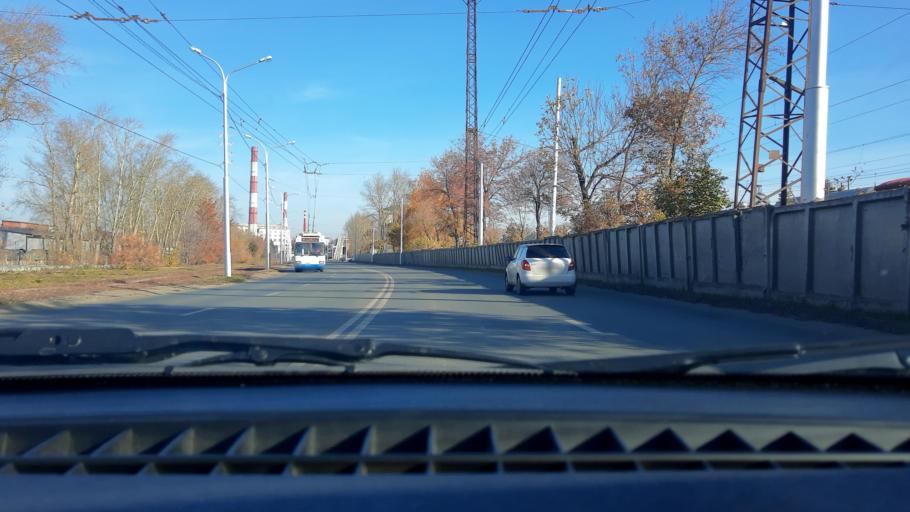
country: RU
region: Bashkortostan
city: Ufa
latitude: 54.8298
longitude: 56.0879
